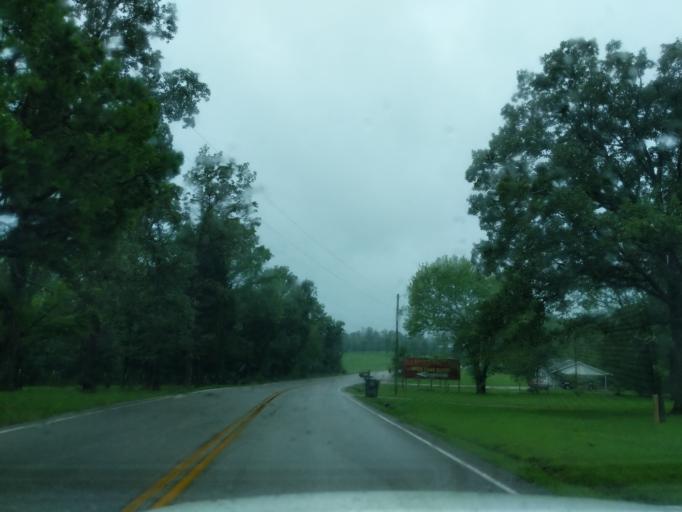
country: US
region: Kentucky
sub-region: Barren County
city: Cave City
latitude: 37.1276
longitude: -86.0536
